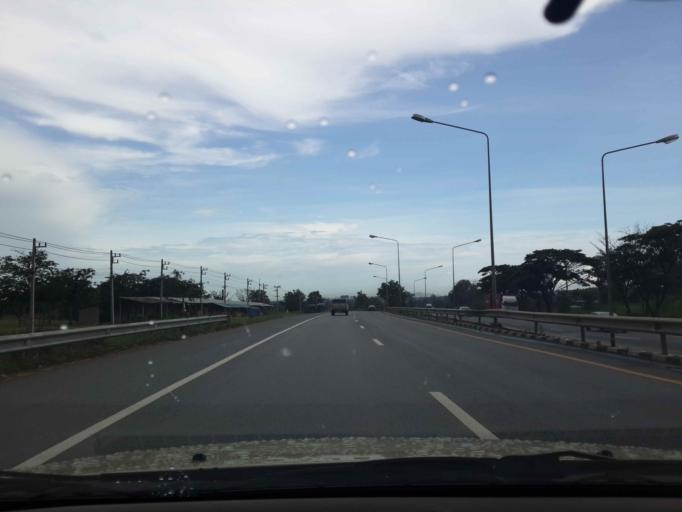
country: TH
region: Chon Buri
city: Phatthaya
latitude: 12.9291
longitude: 101.0022
